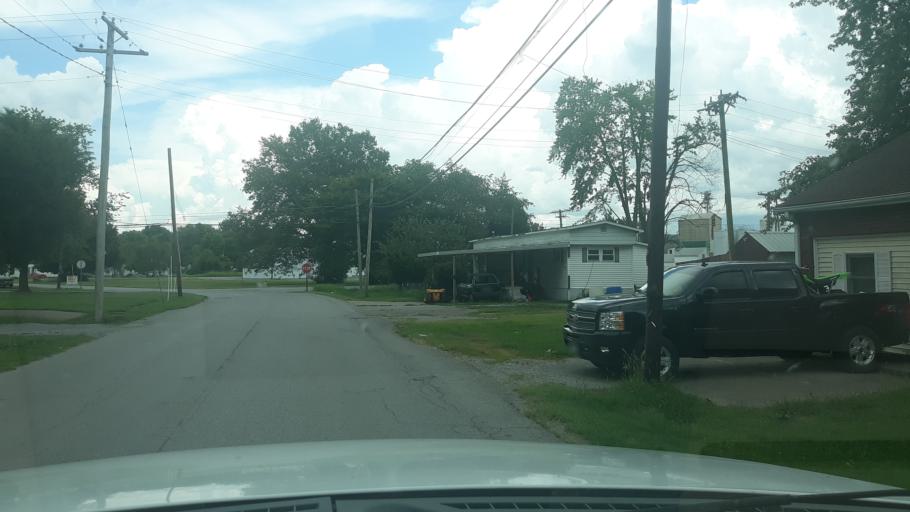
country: US
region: Illinois
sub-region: Saline County
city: Eldorado
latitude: 37.8073
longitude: -88.4530
